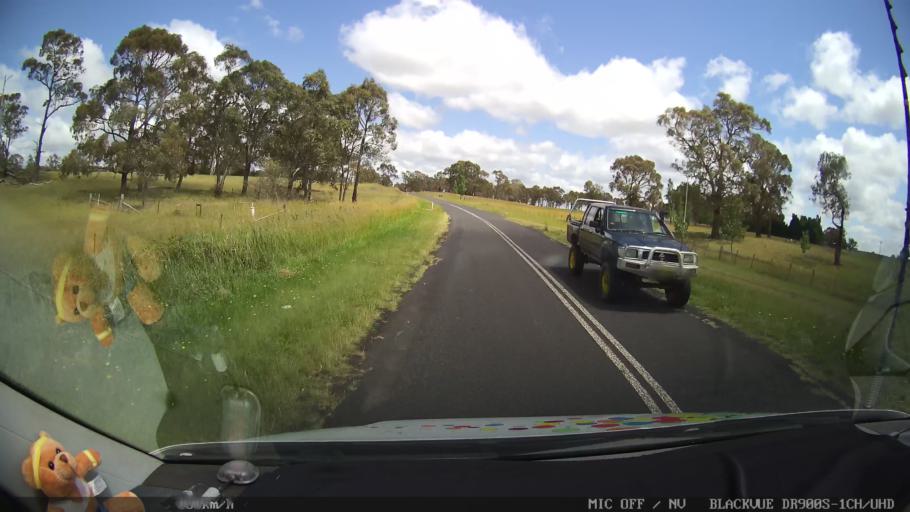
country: AU
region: New South Wales
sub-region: Glen Innes Severn
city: Glen Innes
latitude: -29.6387
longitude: 151.6862
